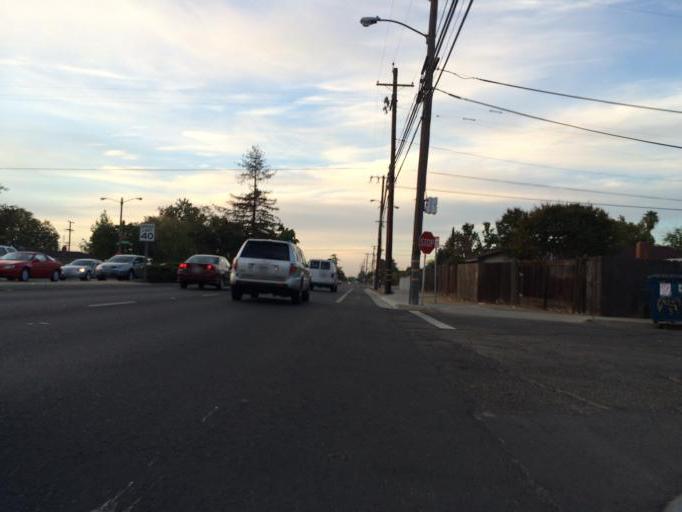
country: US
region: California
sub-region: Fresno County
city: Fresno
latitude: 36.7937
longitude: -119.7544
